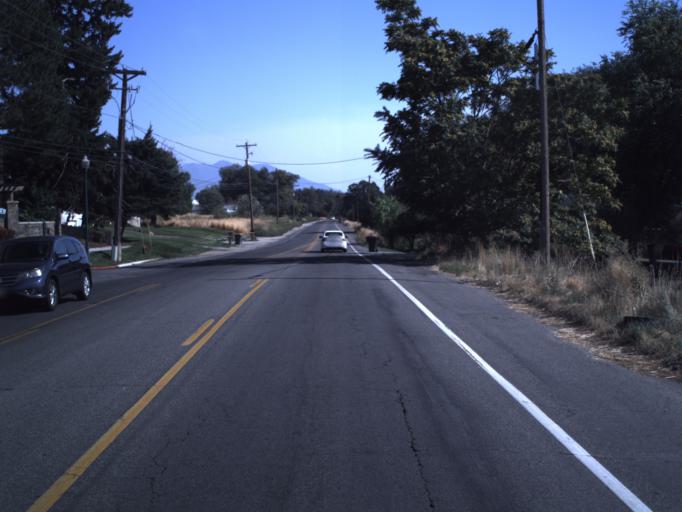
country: US
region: Utah
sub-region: Utah County
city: Orem
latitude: 40.2721
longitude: -111.7248
